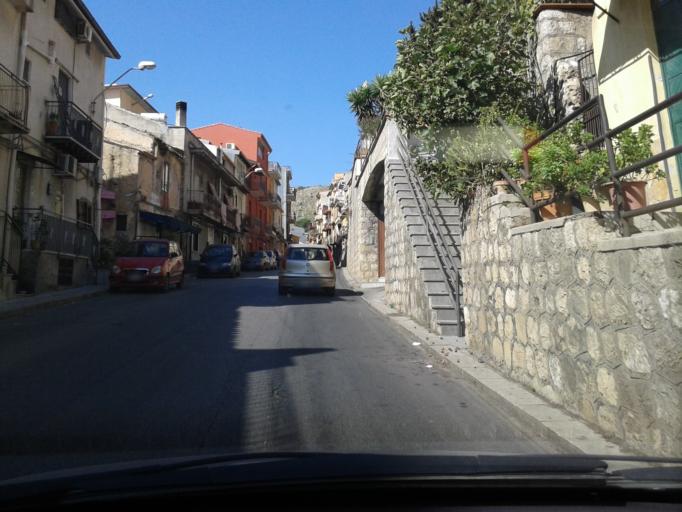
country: IT
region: Sicily
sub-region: Palermo
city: Pioppo
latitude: 38.0465
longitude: 13.2258
